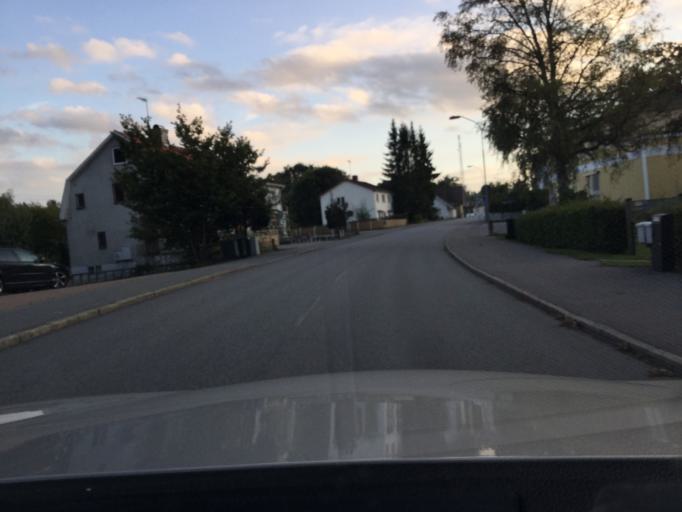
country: SE
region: Kronoberg
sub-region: Almhults Kommun
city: AElmhult
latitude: 56.6368
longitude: 14.2200
